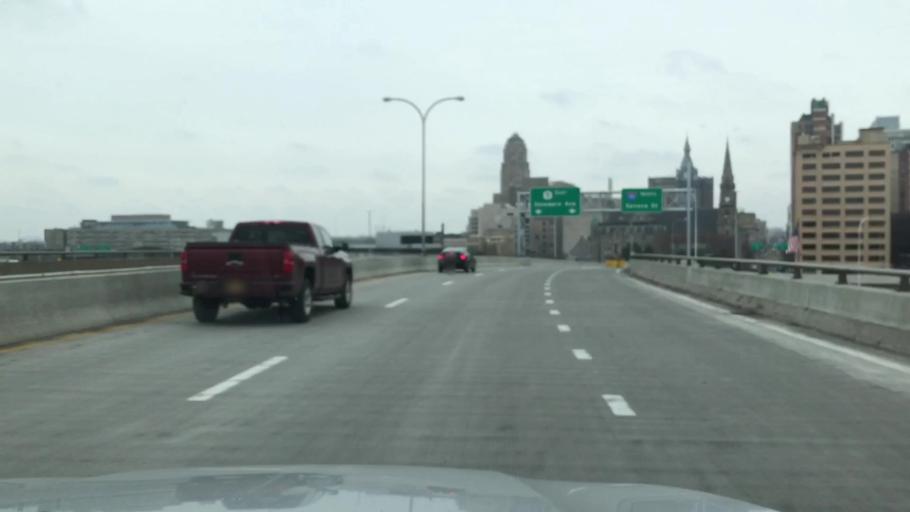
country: US
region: New York
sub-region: Erie County
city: Buffalo
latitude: 42.8793
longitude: -78.8788
